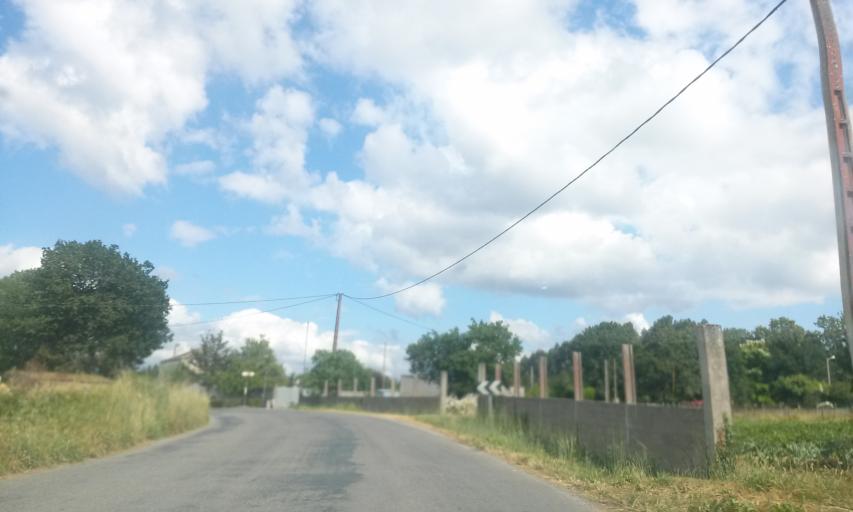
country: ES
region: Galicia
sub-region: Provincia de Lugo
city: Rabade
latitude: 43.1163
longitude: -7.6473
